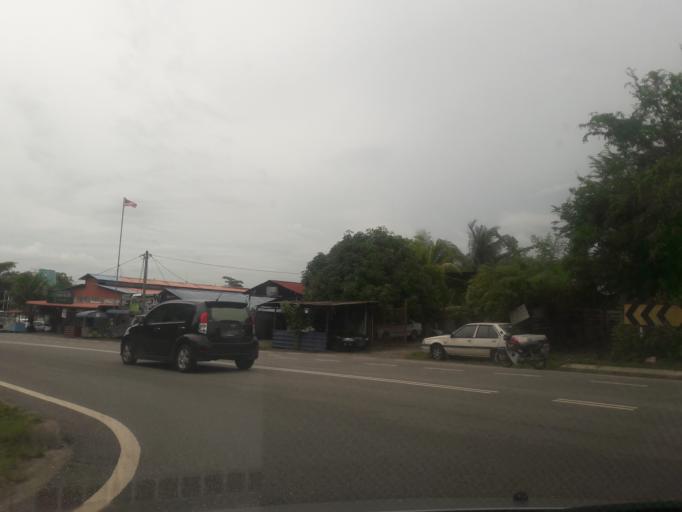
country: MY
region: Kedah
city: Sungai Petani
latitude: 5.6594
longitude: 100.4843
